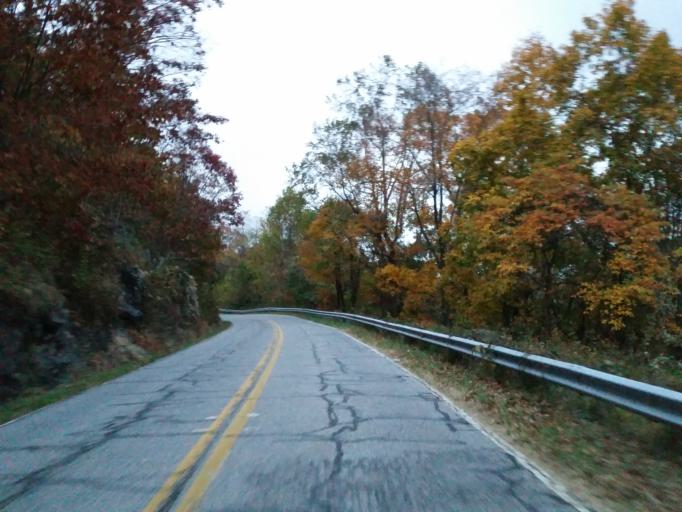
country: US
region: Georgia
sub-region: Lumpkin County
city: Dahlonega
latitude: 34.6766
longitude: -83.9976
